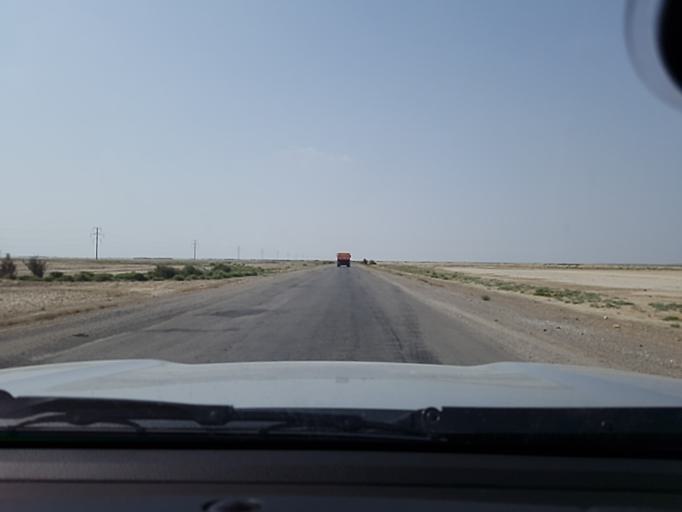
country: TM
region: Balkan
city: Gumdag
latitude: 38.9189
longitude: 54.5912
